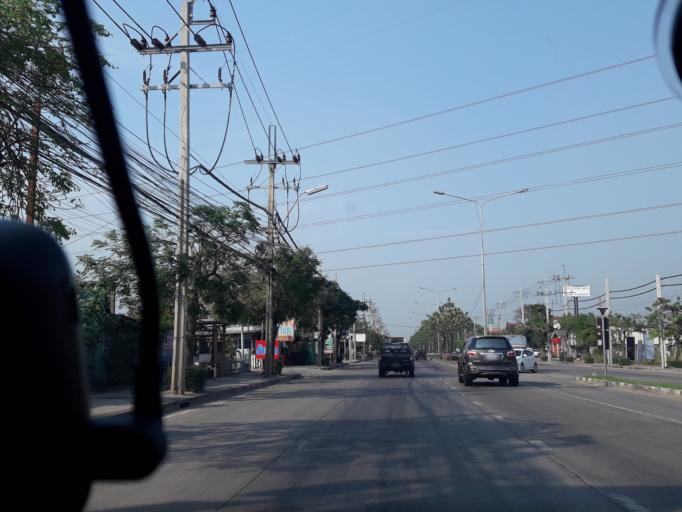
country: TH
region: Bangkok
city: Khlong Sam Wa
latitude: 13.8717
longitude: 100.7318
